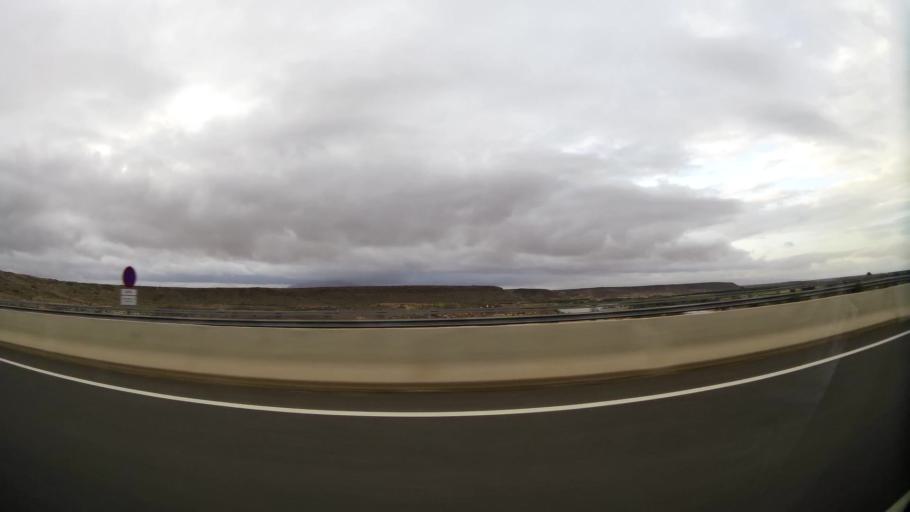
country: MA
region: Taza-Al Hoceima-Taounate
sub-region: Taza
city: Guercif
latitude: 34.3938
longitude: -3.2107
